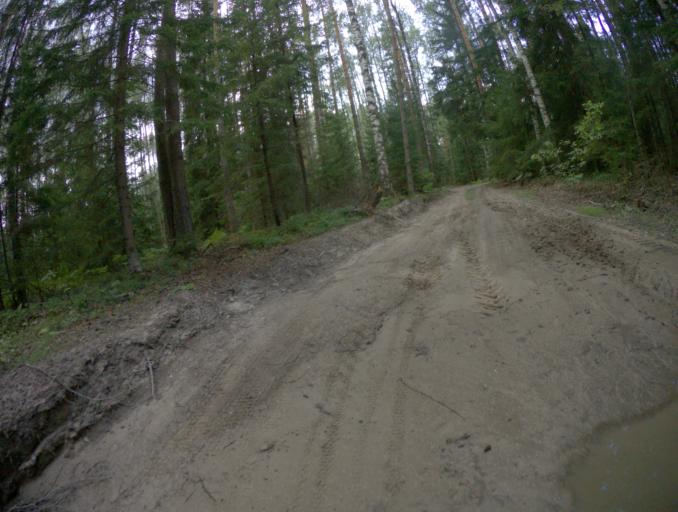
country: RU
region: Vladimir
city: Vorsha
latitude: 55.9509
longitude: 40.1478
